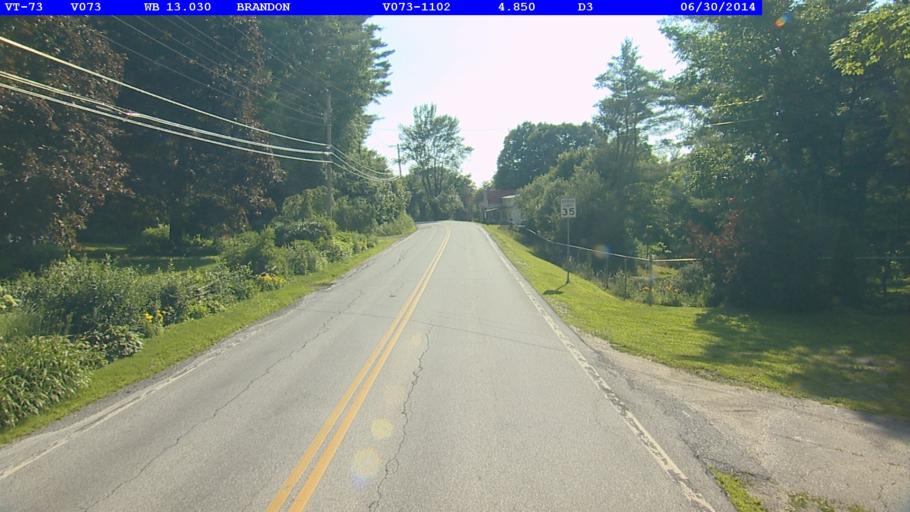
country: US
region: Vermont
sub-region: Rutland County
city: Brandon
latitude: 43.8162
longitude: -73.0670
